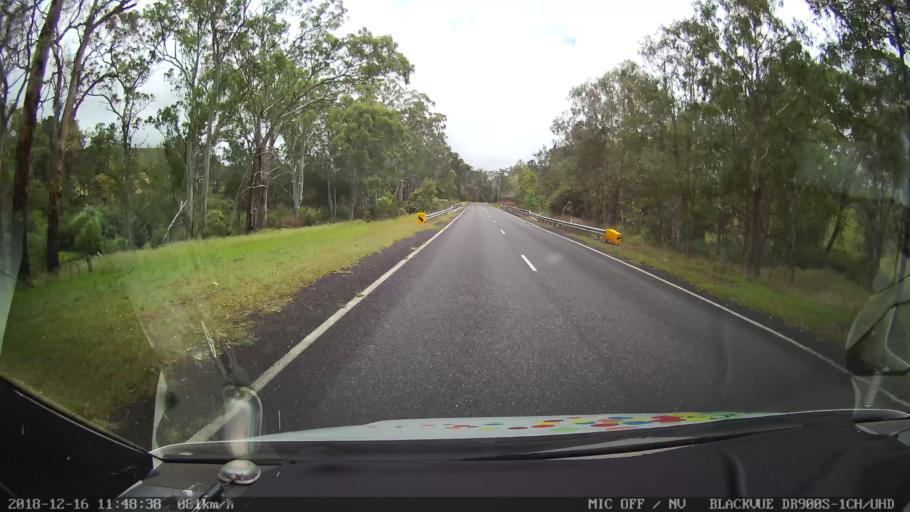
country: AU
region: New South Wales
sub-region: Tenterfield Municipality
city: Carrolls Creek
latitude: -28.9205
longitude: 152.2491
